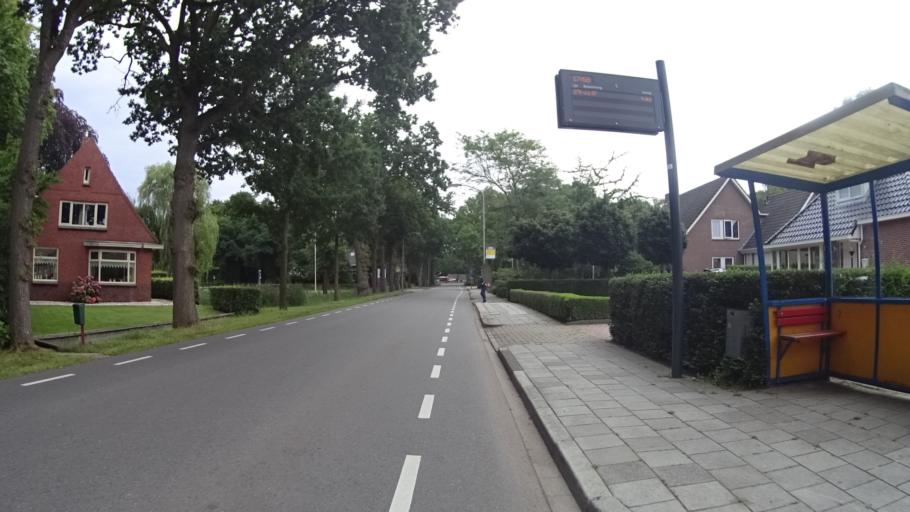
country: NL
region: Groningen
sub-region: Gemeente Slochteren
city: Slochteren
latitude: 53.2201
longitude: 6.8056
